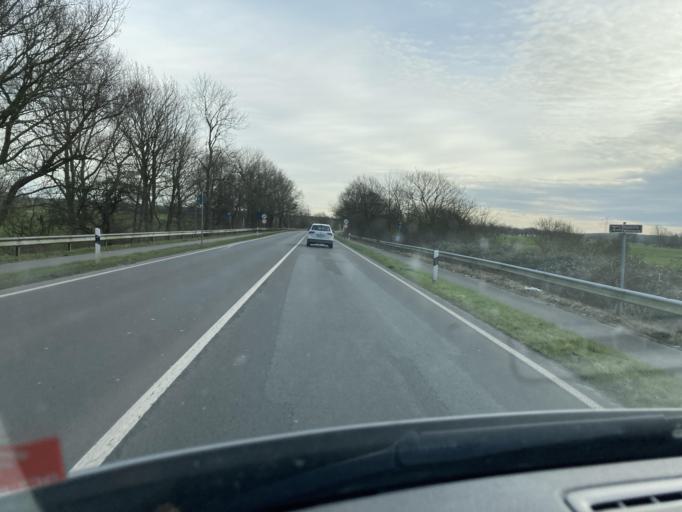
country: DE
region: Lower Saxony
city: Leer
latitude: 53.2191
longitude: 7.4841
